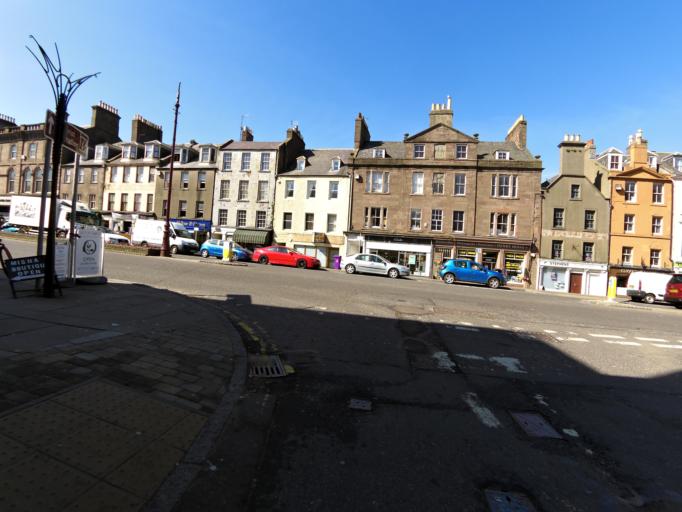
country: GB
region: Scotland
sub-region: Angus
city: Montrose
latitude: 56.7122
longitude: -2.4680
